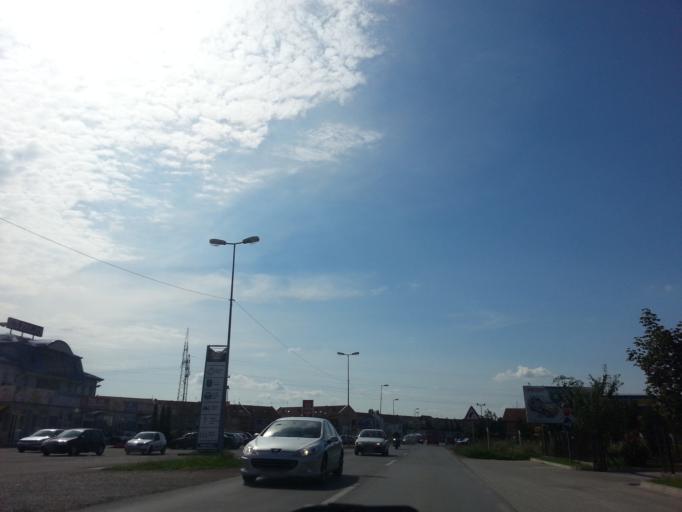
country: BA
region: Brcko
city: Brcko
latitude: 44.8615
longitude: 18.8251
